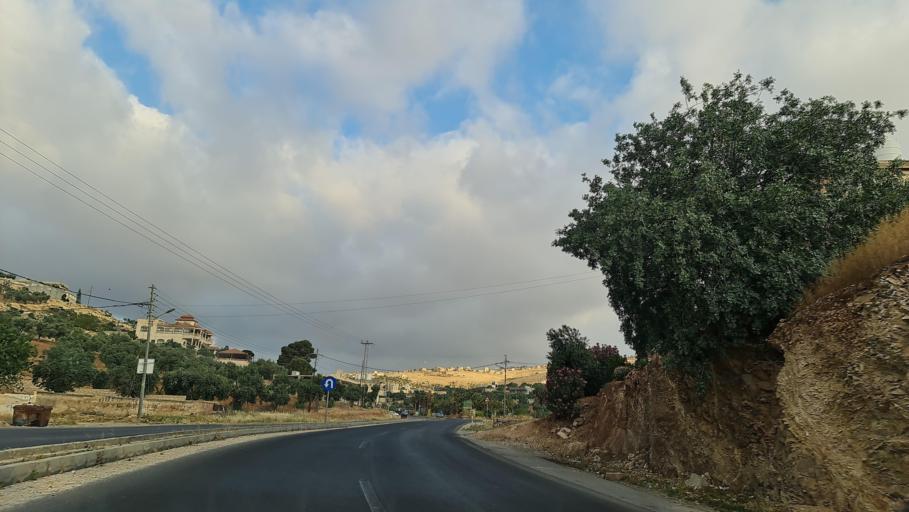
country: JO
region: Amman
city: Al Jubayhah
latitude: 32.0920
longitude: 35.9432
